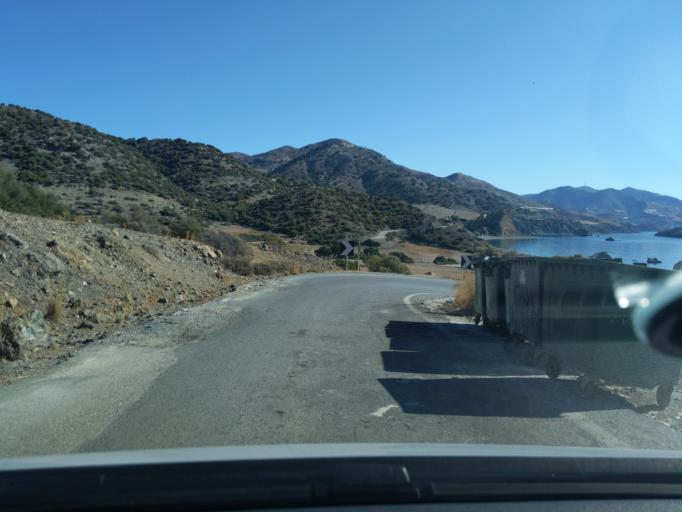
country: GR
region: Crete
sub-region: Nomos Irakleiou
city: Moires
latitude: 34.9344
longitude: 24.8041
